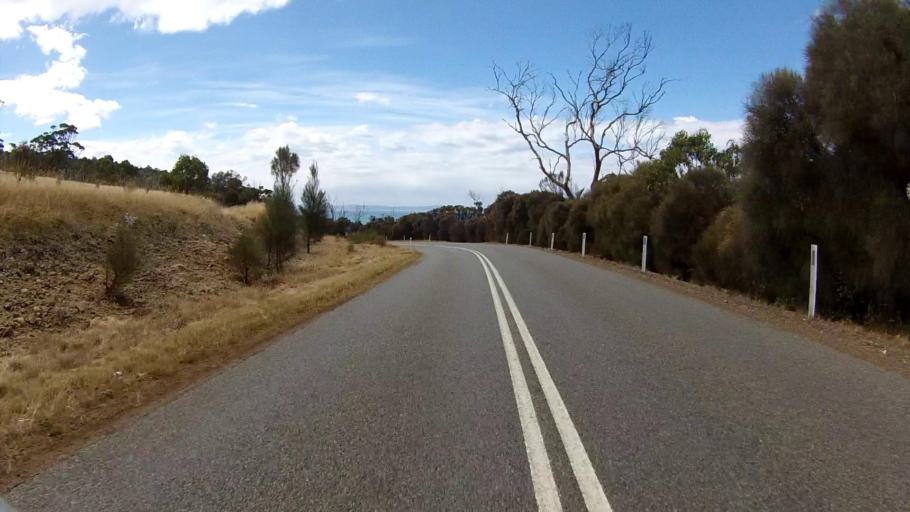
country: AU
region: Tasmania
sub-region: Sorell
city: Sorell
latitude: -42.2328
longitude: 148.0195
